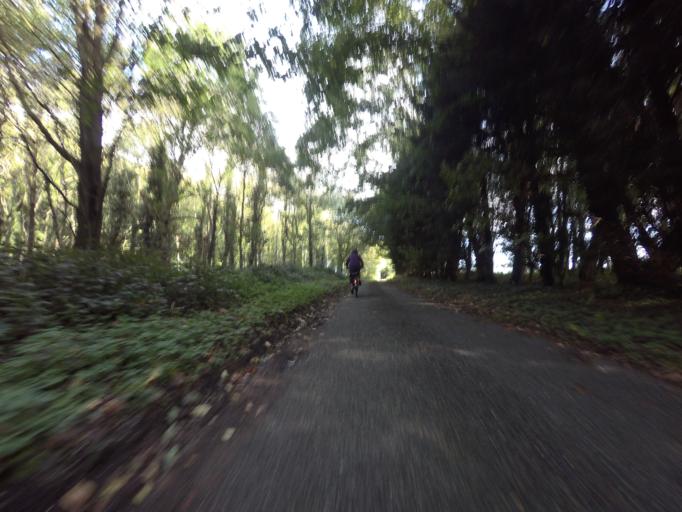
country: GB
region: England
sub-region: Norfolk
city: Dersingham
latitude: 52.8676
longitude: 0.6671
